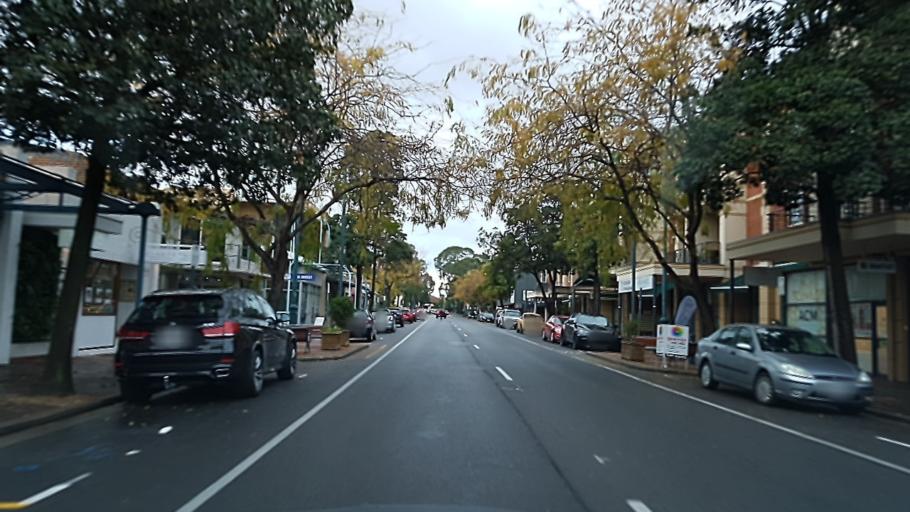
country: AU
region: South Australia
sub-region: Adelaide
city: North Adelaide
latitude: -34.9060
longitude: 138.6088
